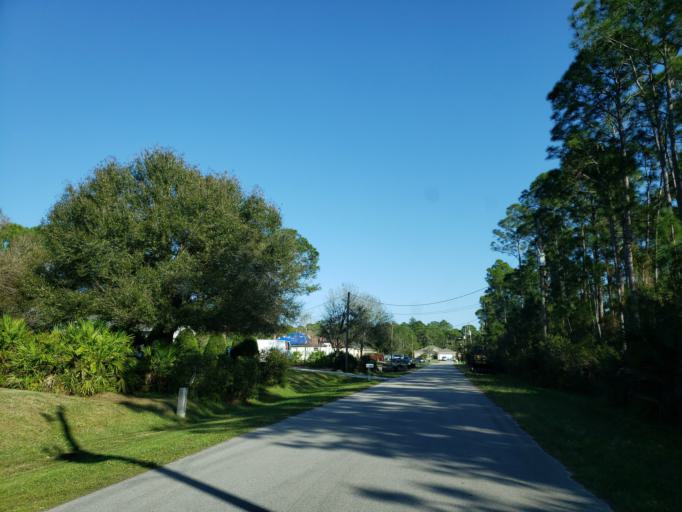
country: US
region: Florida
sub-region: Sarasota County
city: North Port
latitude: 27.0806
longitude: -82.1970
